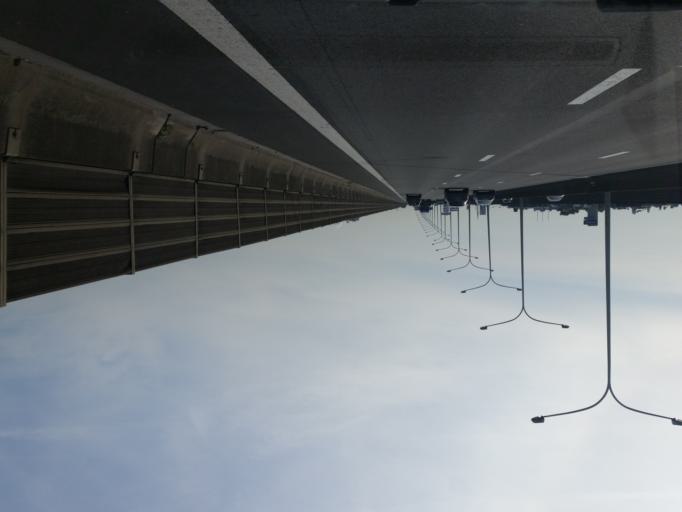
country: BE
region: Flanders
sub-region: Provincie Antwerpen
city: Aartselaar
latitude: 51.1692
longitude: 4.3865
